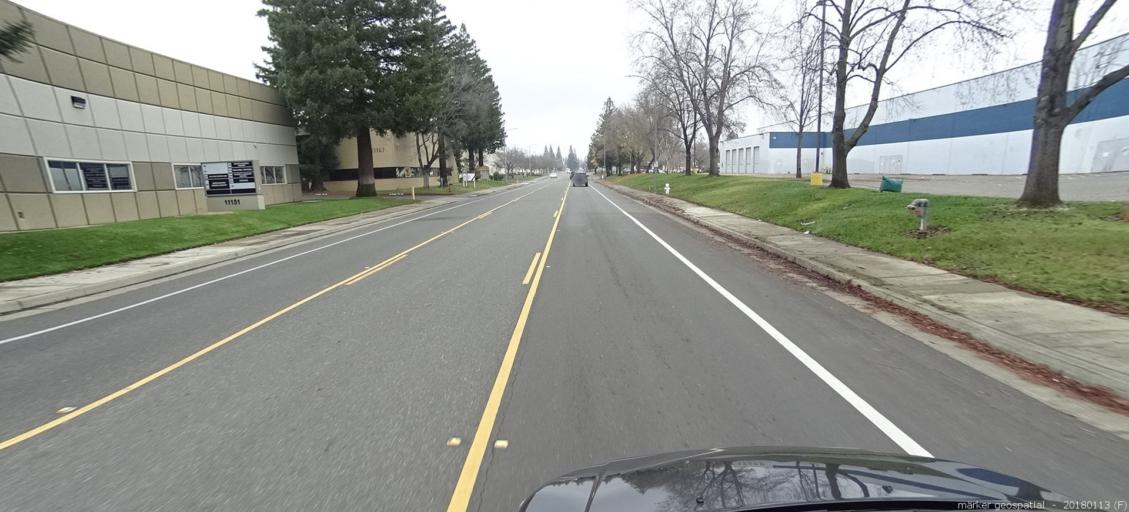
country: US
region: California
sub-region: Sacramento County
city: Gold River
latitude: 38.6021
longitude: -121.2706
